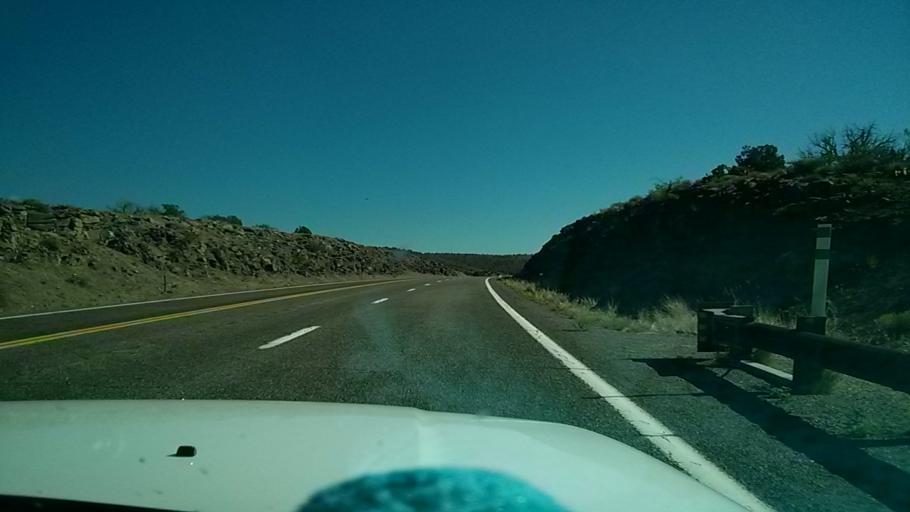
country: US
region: Arizona
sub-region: Mohave County
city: Peach Springs
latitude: 35.4323
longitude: -113.6488
